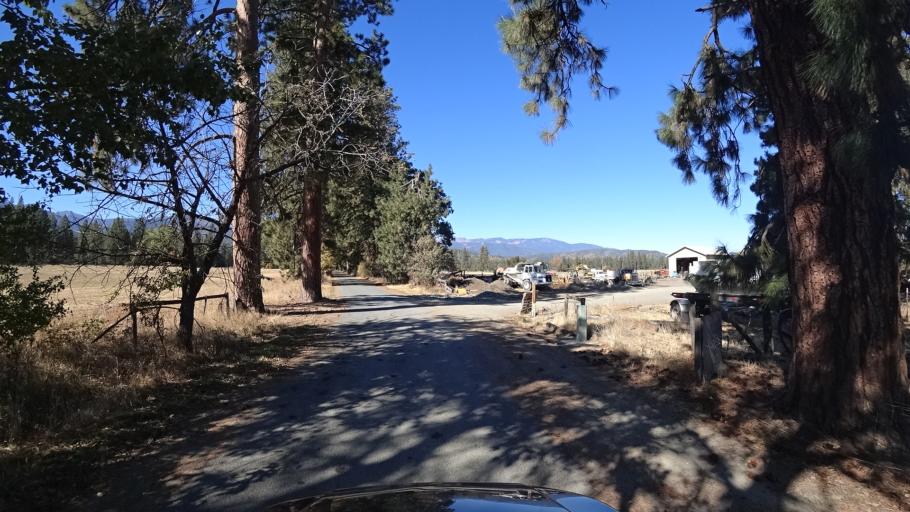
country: US
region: California
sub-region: Siskiyou County
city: Yreka
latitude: 41.5247
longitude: -122.9017
